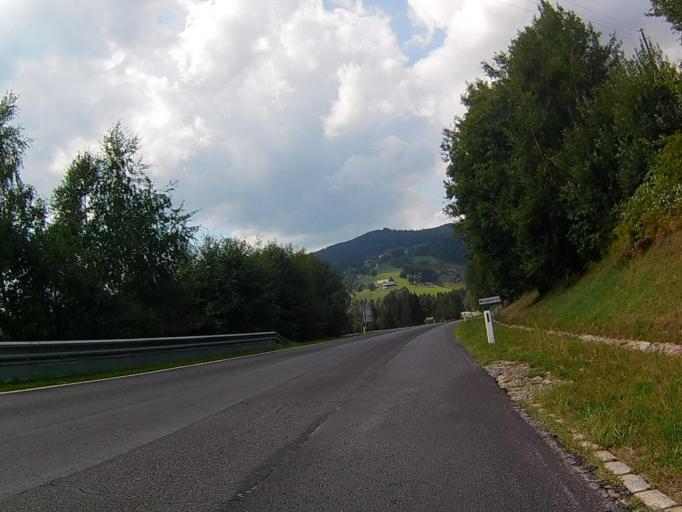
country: AT
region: Styria
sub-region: Politischer Bezirk Deutschlandsberg
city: Soboth
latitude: 46.6826
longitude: 15.0705
